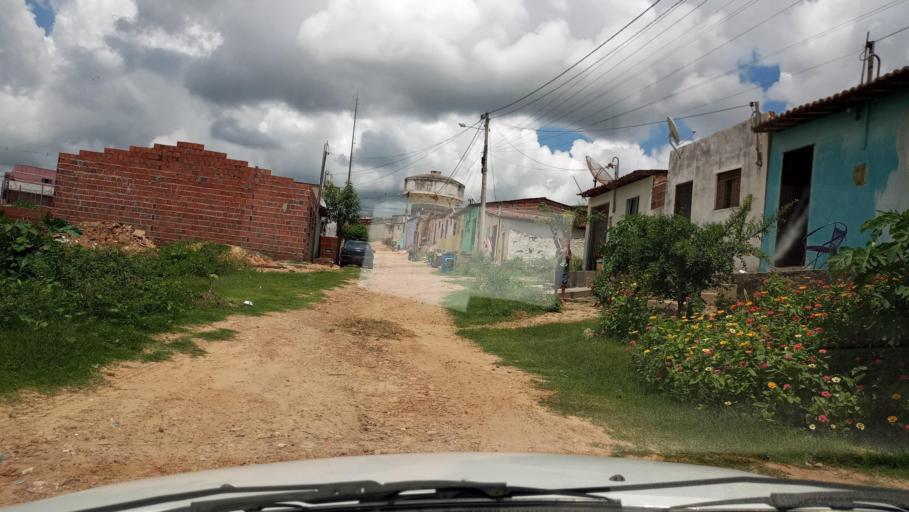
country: BR
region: Rio Grande do Norte
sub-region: Sao Paulo Do Potengi
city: Sao Paulo do Potengi
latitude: -5.8980
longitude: -35.7716
